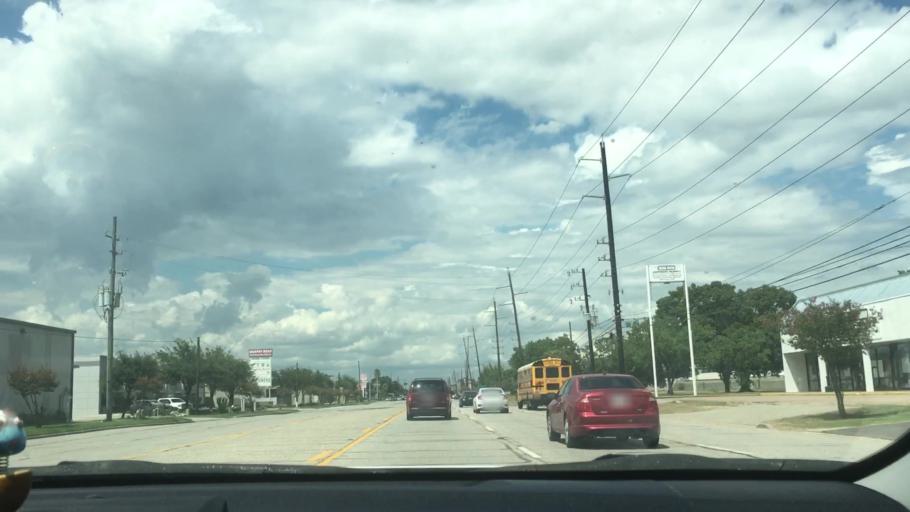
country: US
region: Texas
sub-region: Fort Bend County
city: Stafford
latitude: 29.6294
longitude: -95.5649
